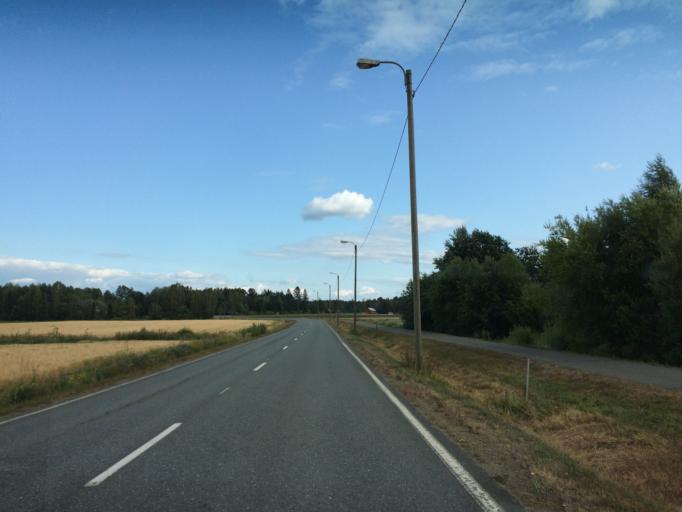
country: FI
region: Haeme
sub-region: Haemeenlinna
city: Tuulos
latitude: 61.0669
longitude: 24.6856
